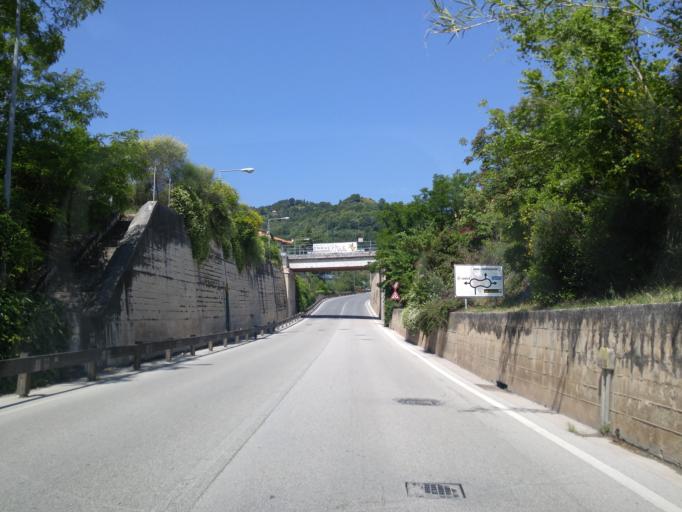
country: IT
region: The Marches
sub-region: Provincia di Pesaro e Urbino
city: Fossombrone
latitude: 43.6923
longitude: 12.8224
